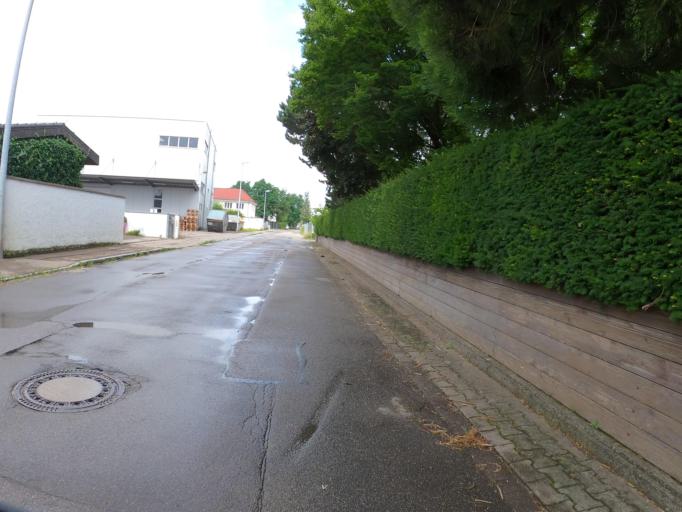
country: DE
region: Baden-Wuerttemberg
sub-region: Tuebingen Region
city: Langenau
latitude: 48.4905
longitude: 10.1246
